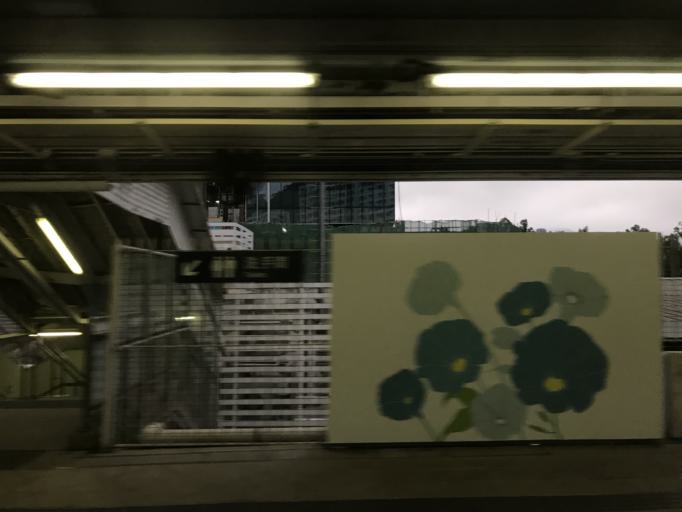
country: HK
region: Sha Tin
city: Sha Tin
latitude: 22.4135
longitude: 114.2101
